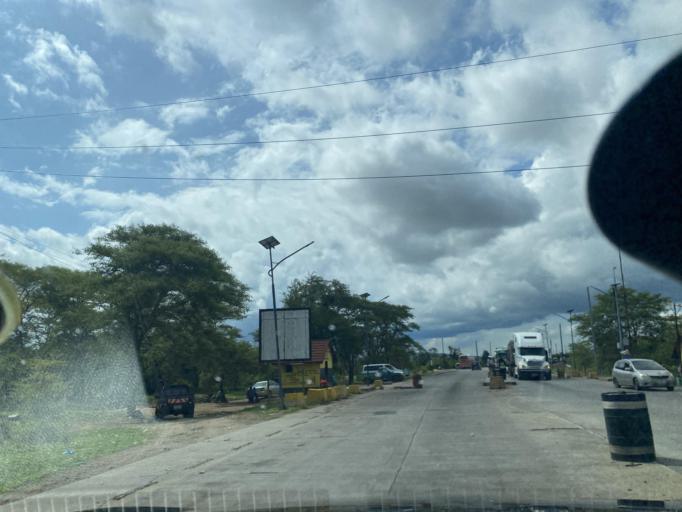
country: ZM
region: Lusaka
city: Kafue
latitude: -15.8439
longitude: 28.2410
